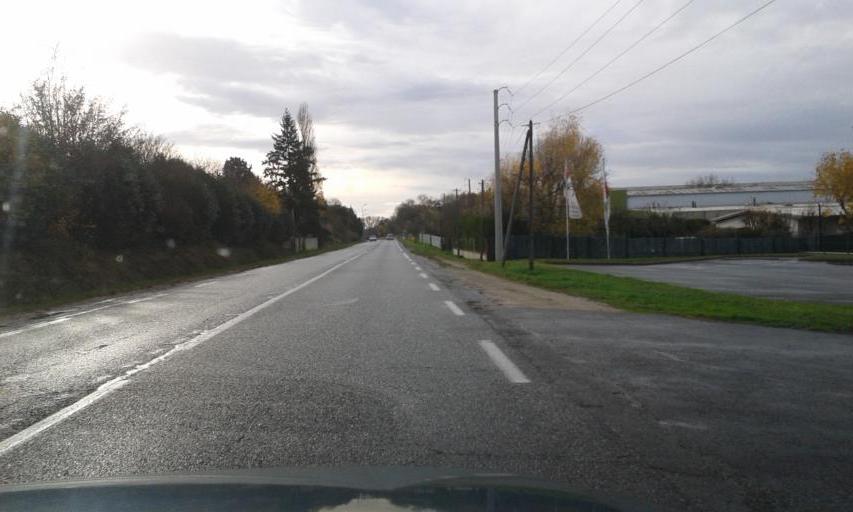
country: FR
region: Centre
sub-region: Departement du Loiret
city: Meung-sur-Loire
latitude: 47.8406
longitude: 1.7145
